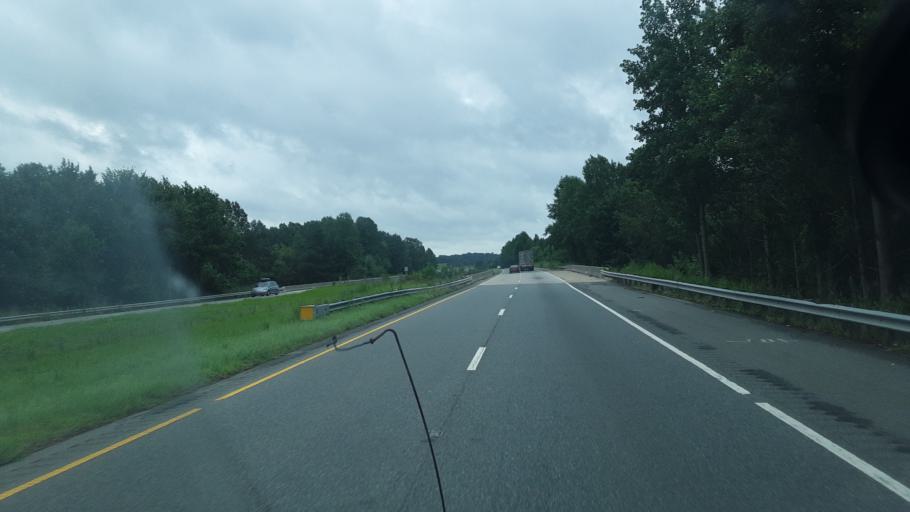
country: US
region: North Carolina
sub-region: Montgomery County
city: Biscoe
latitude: 35.5038
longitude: -79.7814
